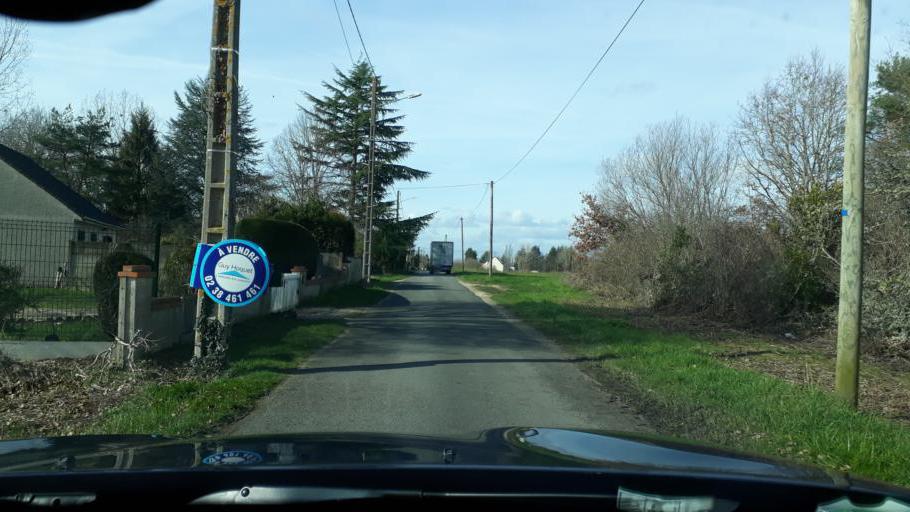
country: FR
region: Centre
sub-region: Departement du Loiret
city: Donnery
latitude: 47.9102
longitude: 2.1145
